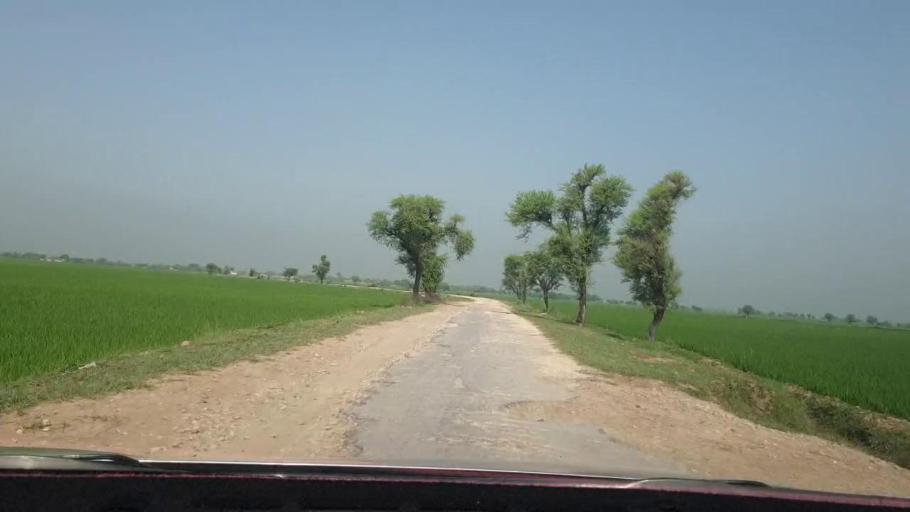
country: PK
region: Sindh
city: Nasirabad
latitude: 27.4296
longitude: 67.9025
